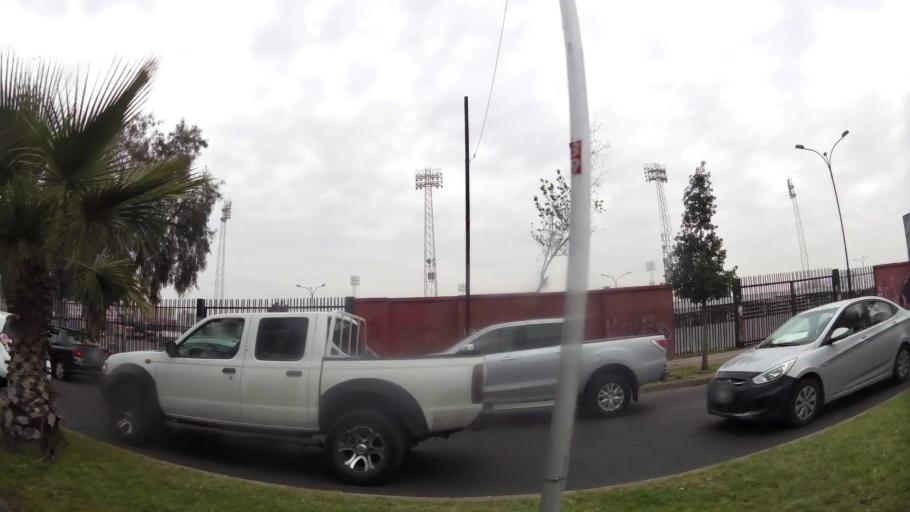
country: CL
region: Santiago Metropolitan
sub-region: Provincia de Santiago
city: Villa Presidente Frei, Nunoa, Santiago, Chile
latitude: -33.5070
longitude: -70.6040
